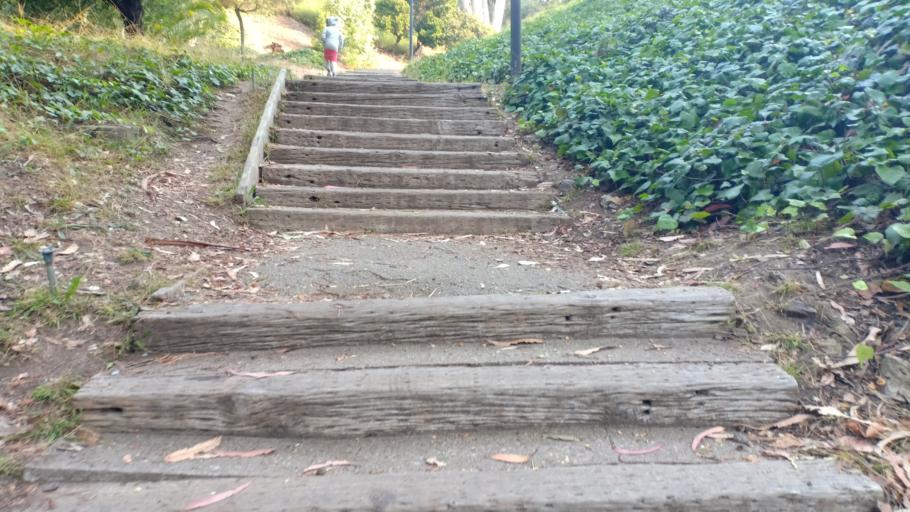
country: US
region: California
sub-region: Alameda County
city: Berkeley
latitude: 37.8850
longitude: -122.2559
